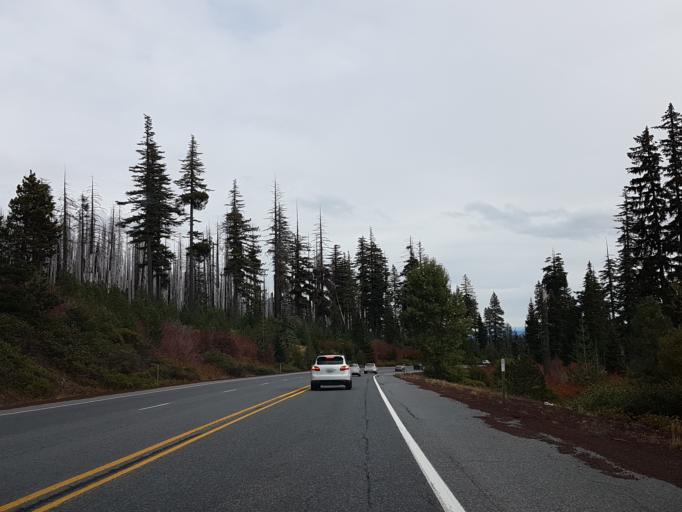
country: US
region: Oregon
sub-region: Deschutes County
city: Sisters
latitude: 44.4231
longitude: -121.7949
